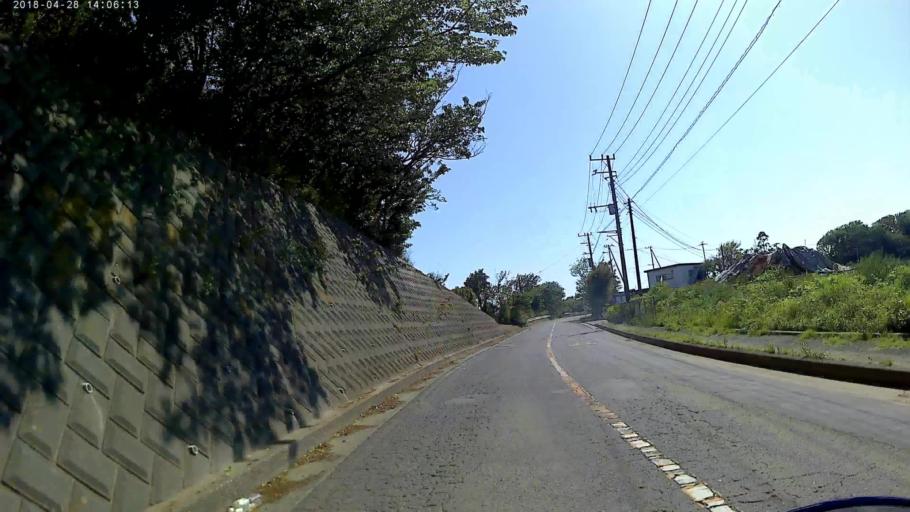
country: JP
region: Kanagawa
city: Miura
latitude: 35.1572
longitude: 139.6479
